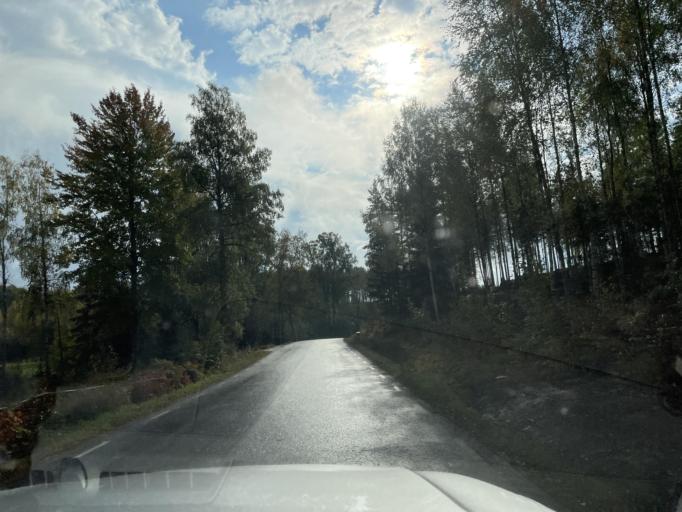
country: SE
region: Vaermland
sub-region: Karlstads Kommun
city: Skattkarr
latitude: 59.4229
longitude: 13.6056
